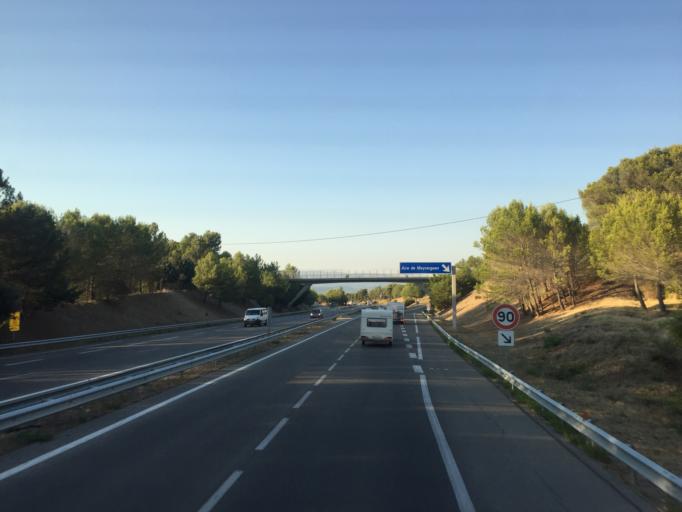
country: FR
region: Provence-Alpes-Cote d'Azur
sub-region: Departement des Bouches-du-Rhone
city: Venelles
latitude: 43.6281
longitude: 5.4930
